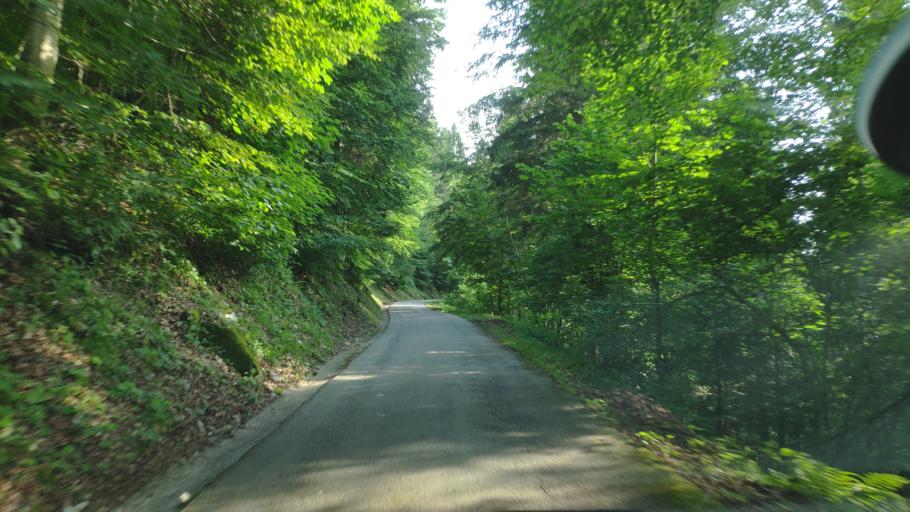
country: IT
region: Veneto
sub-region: Provincia di Vicenza
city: Cogollo del Cengio
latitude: 45.8165
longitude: 11.4375
